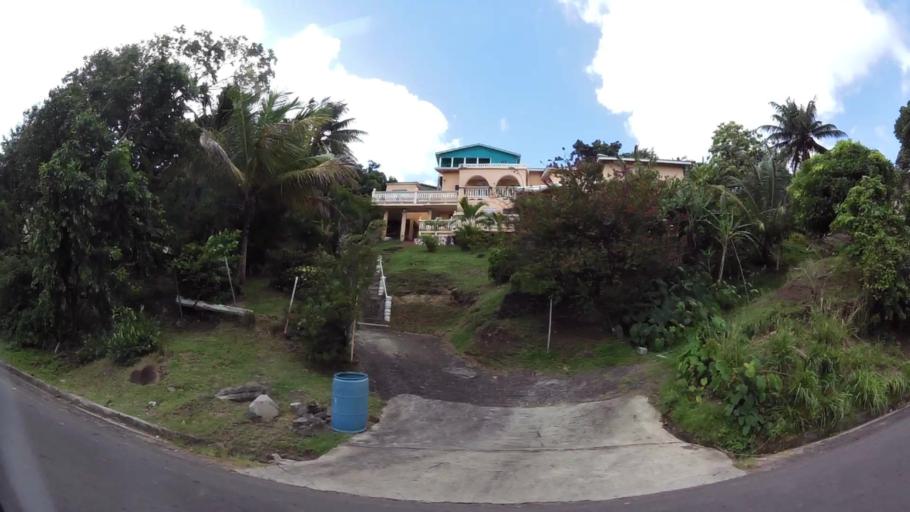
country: LC
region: Laborie Quarter
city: Laborie
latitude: 13.7512
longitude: -60.9887
